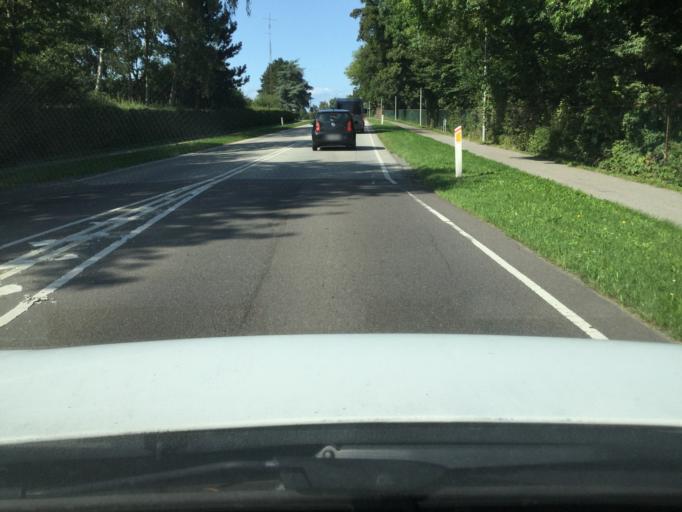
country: DK
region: Zealand
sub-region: Lolland Kommune
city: Nakskov
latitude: 54.8188
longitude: 11.1571
